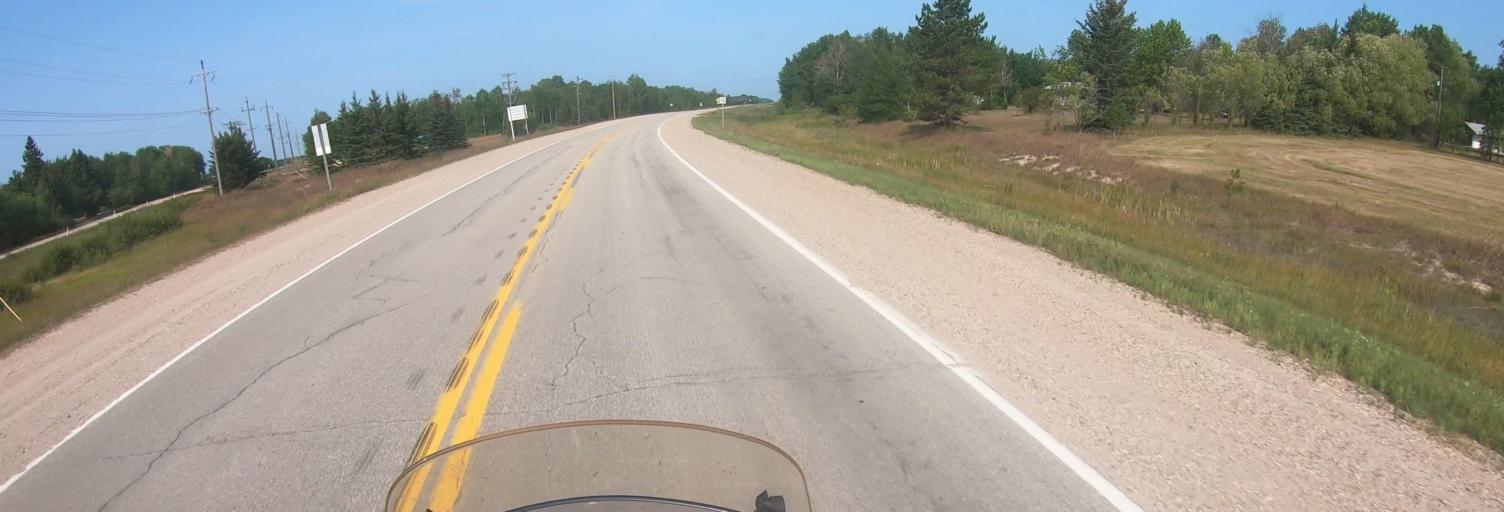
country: US
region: Minnesota
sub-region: Roseau County
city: Roseau
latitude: 49.0900
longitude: -95.9800
